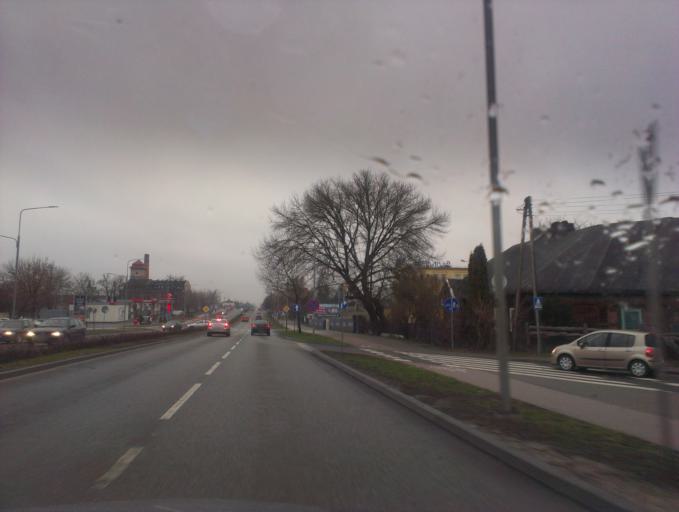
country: PL
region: Masovian Voivodeship
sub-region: Radom
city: Radom
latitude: 51.4158
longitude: 21.1538
